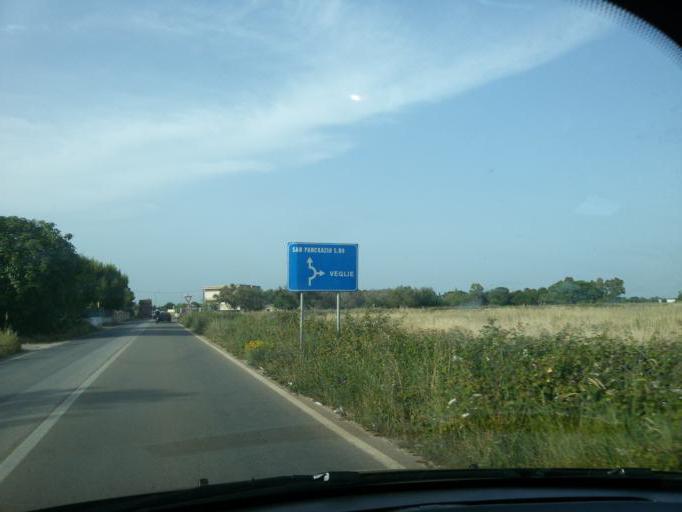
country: IT
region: Apulia
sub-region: Provincia di Lecce
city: Porto Cesareo
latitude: 40.3006
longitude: 17.8585
